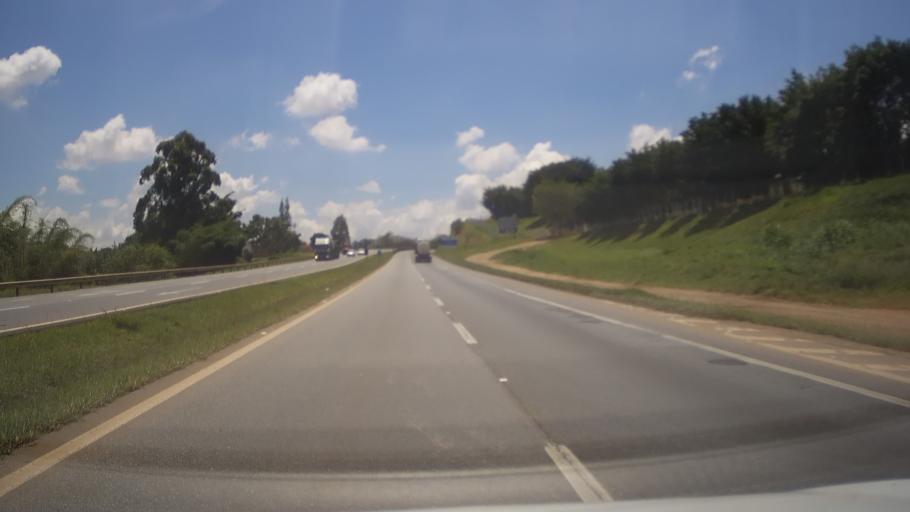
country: BR
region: Minas Gerais
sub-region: Sao Goncalo Do Sapucai
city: Sao Goncalo do Sapucai
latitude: -21.9113
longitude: -45.5737
